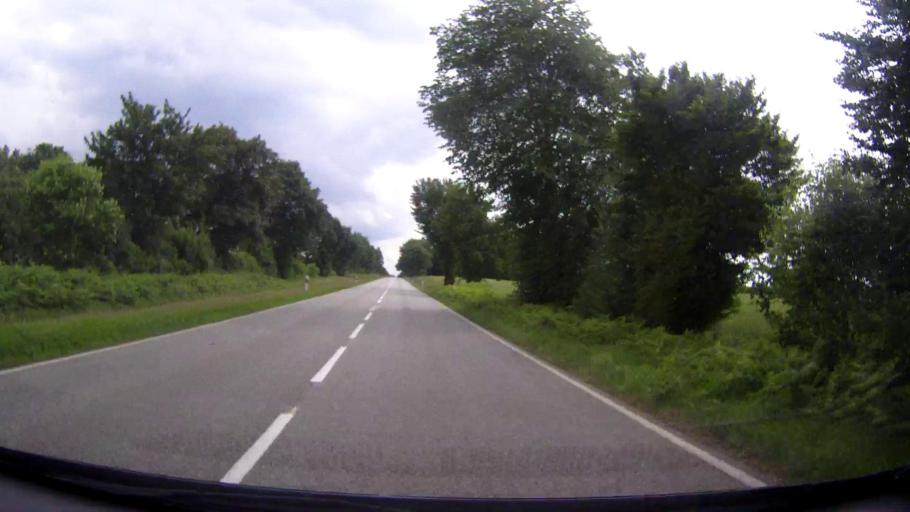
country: DE
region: Schleswig-Holstein
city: Warringholz
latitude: 54.0898
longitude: 9.4657
